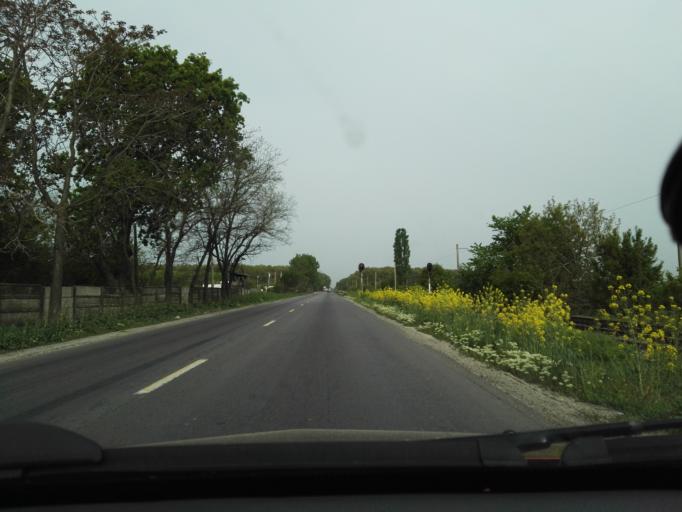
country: RO
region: Ilfov
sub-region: Comuna Magurele
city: Alunisu
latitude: 44.3501
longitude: 26.0648
